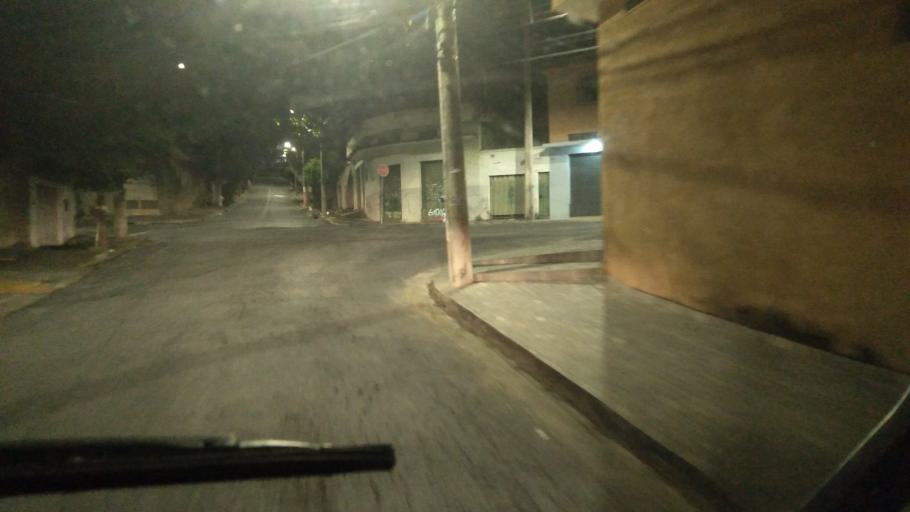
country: BR
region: Minas Gerais
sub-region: Belo Horizonte
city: Belo Horizonte
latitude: -19.8754
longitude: -43.9401
